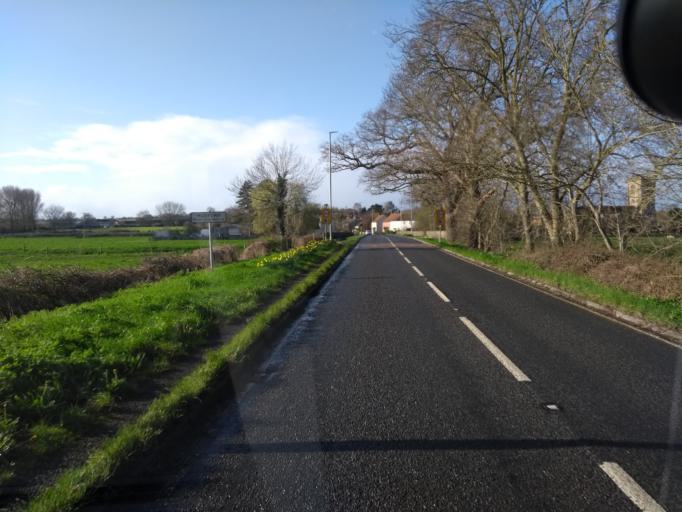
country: GB
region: England
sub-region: Somerset
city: Yeovil
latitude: 50.9783
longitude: -2.6062
